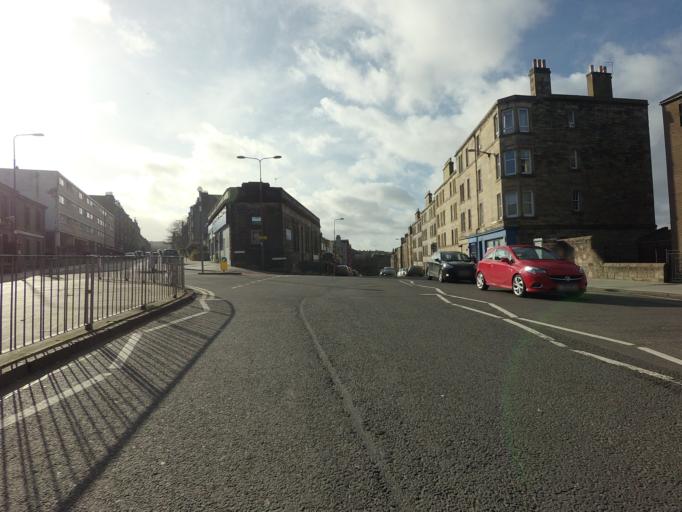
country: GB
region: Scotland
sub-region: Edinburgh
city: Edinburgh
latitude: 55.9655
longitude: -3.1896
